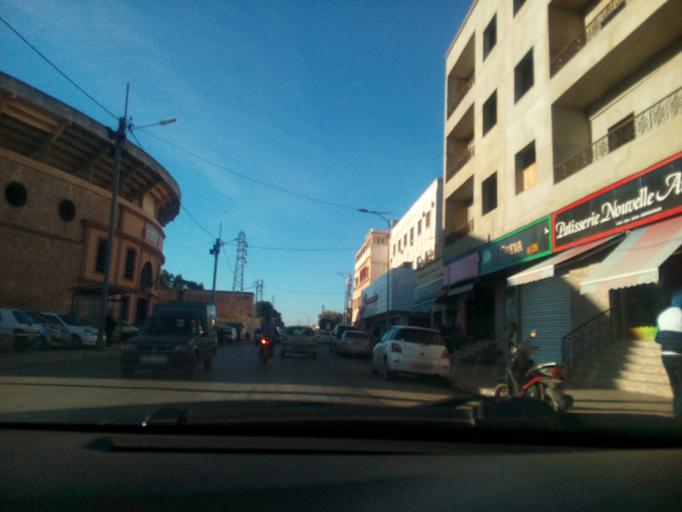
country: DZ
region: Oran
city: Oran
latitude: 35.6863
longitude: -0.6667
